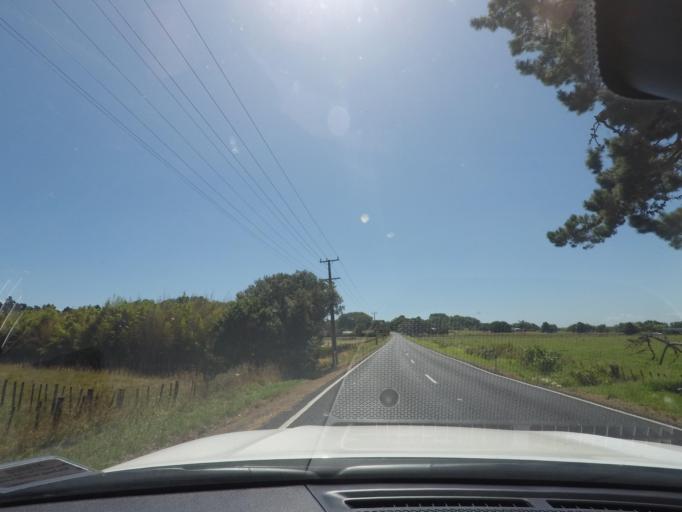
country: NZ
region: Auckland
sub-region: Auckland
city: Parakai
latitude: -36.6487
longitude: 174.4036
